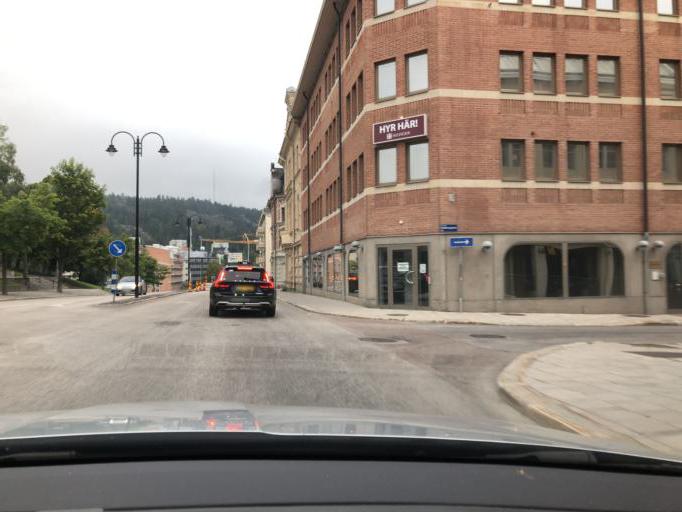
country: SE
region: Vaesternorrland
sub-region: Sundsvalls Kommun
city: Sundsvall
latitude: 62.3898
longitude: 17.3009
